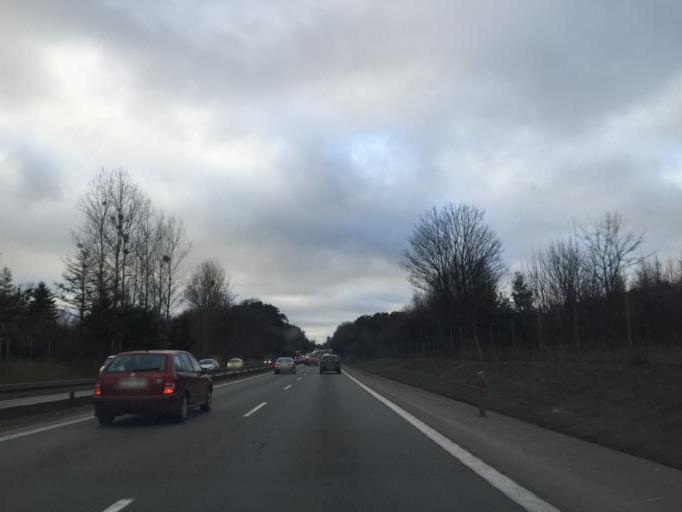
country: PL
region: Pomeranian Voivodeship
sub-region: Gdynia
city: Wielki Kack
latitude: 54.3870
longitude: 18.4996
